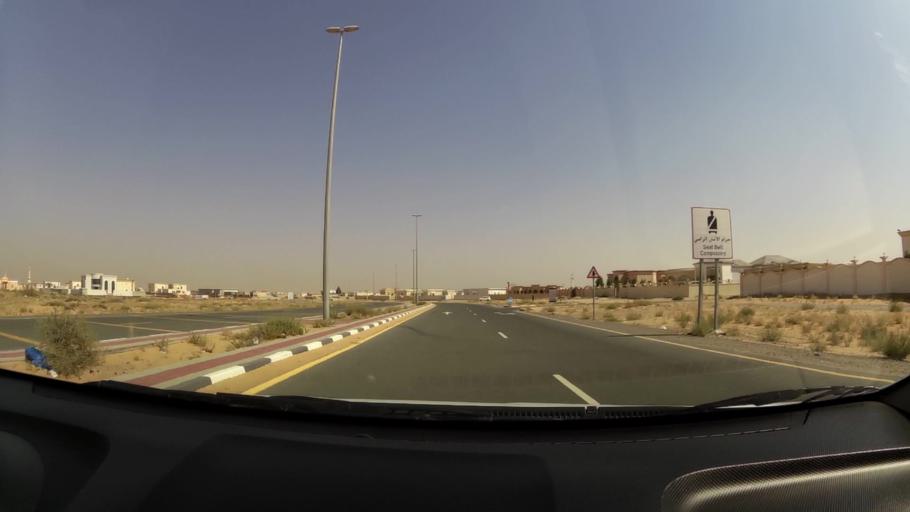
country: AE
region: Umm al Qaywayn
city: Umm al Qaywayn
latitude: 25.4775
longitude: 55.6046
